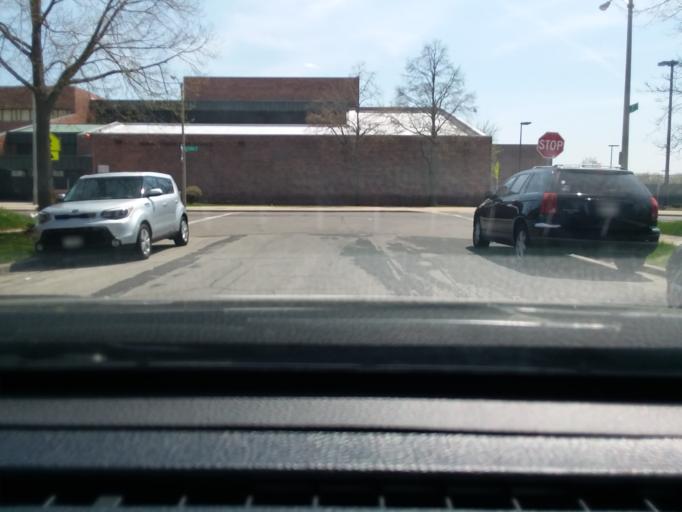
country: US
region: Wisconsin
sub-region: Milwaukee County
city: Milwaukee
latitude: 43.0679
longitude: -87.9255
